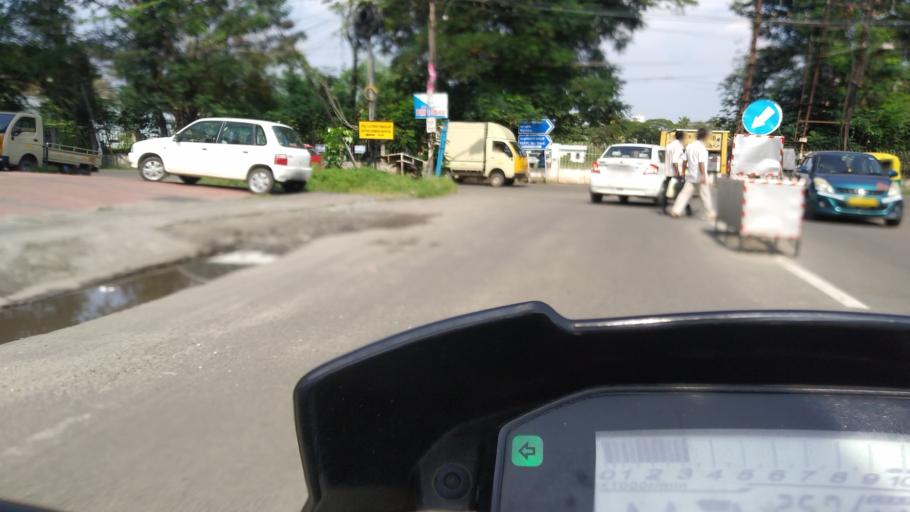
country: IN
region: Kerala
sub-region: Ernakulam
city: Cochin
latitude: 9.9789
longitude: 76.2870
